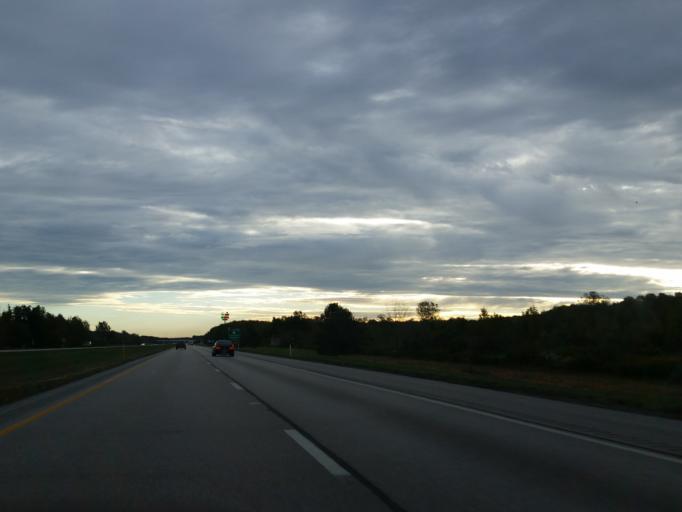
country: US
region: Ohio
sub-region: Ashtabula County
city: Conneaut
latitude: 41.9124
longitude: -80.5854
